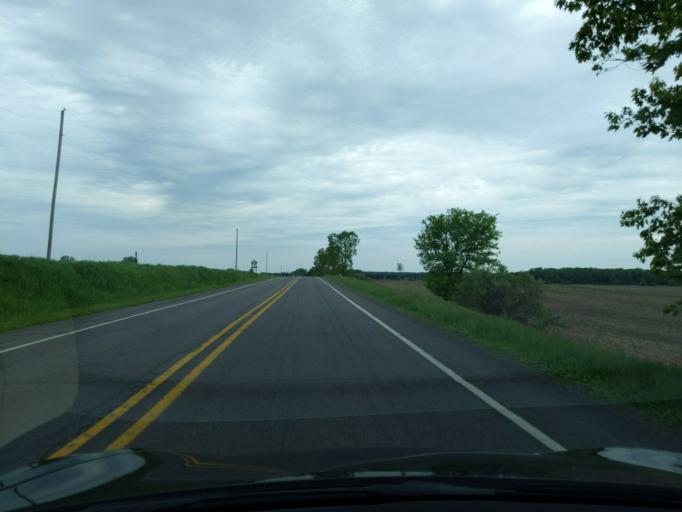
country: US
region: Michigan
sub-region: Ingham County
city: Mason
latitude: 42.5858
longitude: -84.3573
